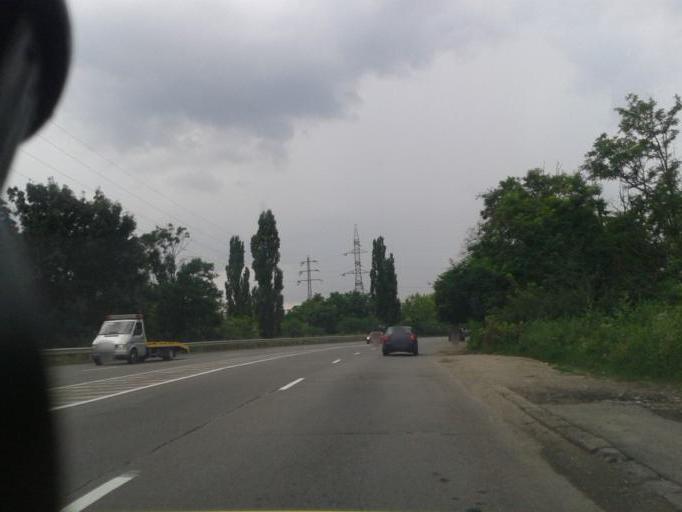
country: RO
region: Prahova
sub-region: Comuna Bucov
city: Bucov
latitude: 44.9633
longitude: 26.0606
